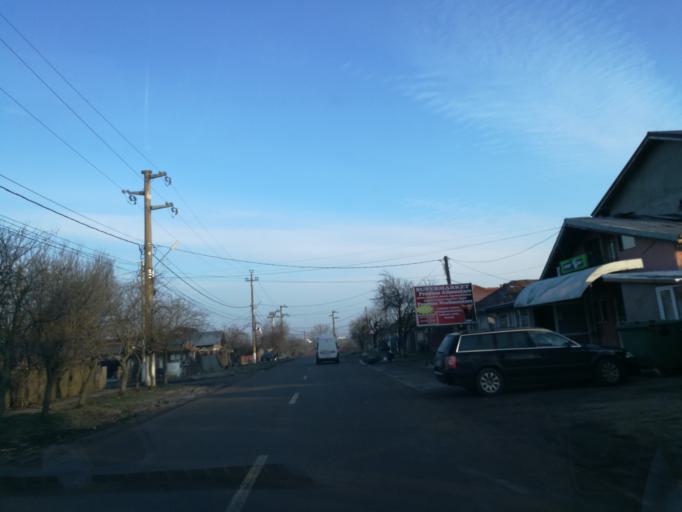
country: RO
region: Ilfov
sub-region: Comuna Moara Vlasiei
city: Caciulati
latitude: 44.6304
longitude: 26.1773
